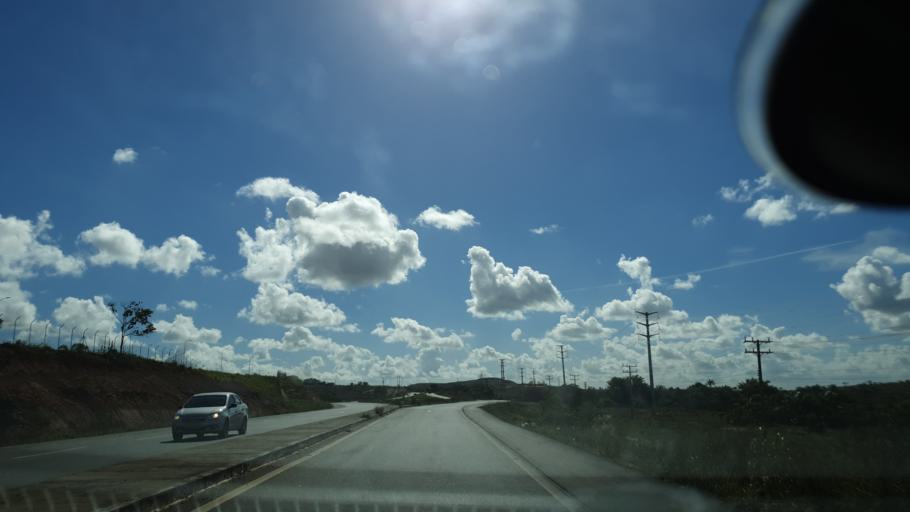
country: BR
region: Bahia
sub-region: Camacari
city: Camacari
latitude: -12.6826
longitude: -38.2457
